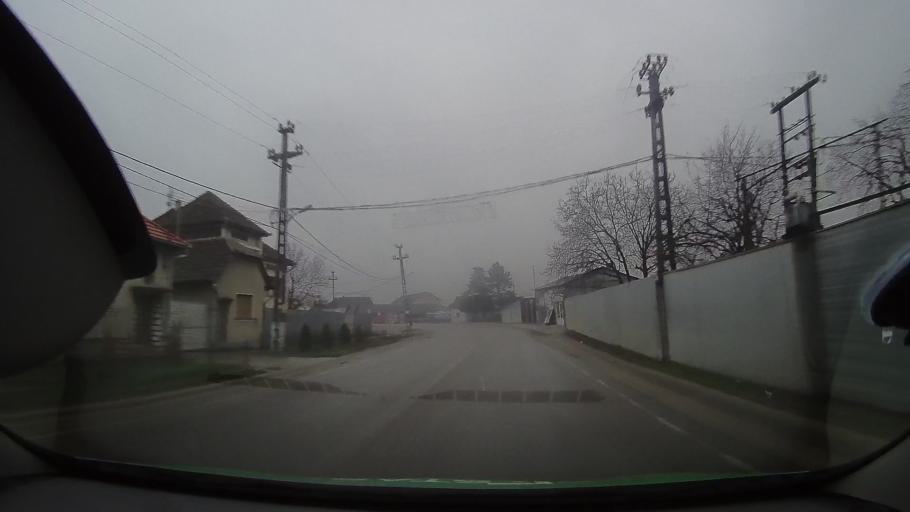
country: RO
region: Bihor
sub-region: Comuna Tinca
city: Tinca
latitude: 46.7723
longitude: 21.9302
